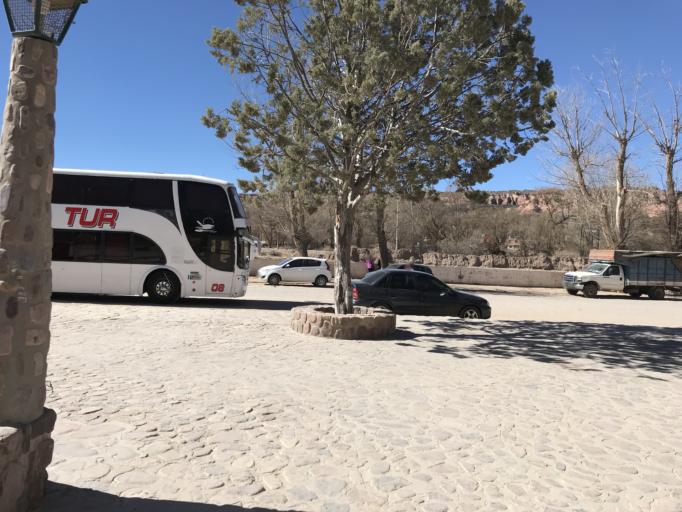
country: AR
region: Jujuy
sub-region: Departamento de Humahuaca
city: Humahuaca
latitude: -23.2042
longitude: -65.3460
